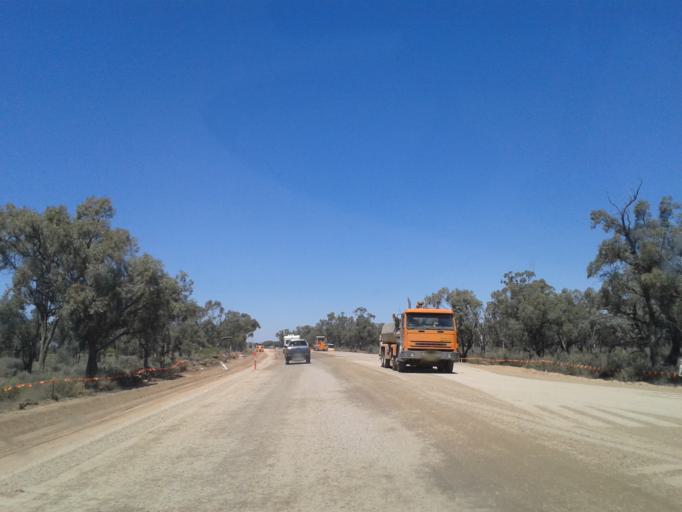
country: AU
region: New South Wales
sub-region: Wentworth
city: Gol Gol
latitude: -34.5628
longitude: 142.7260
